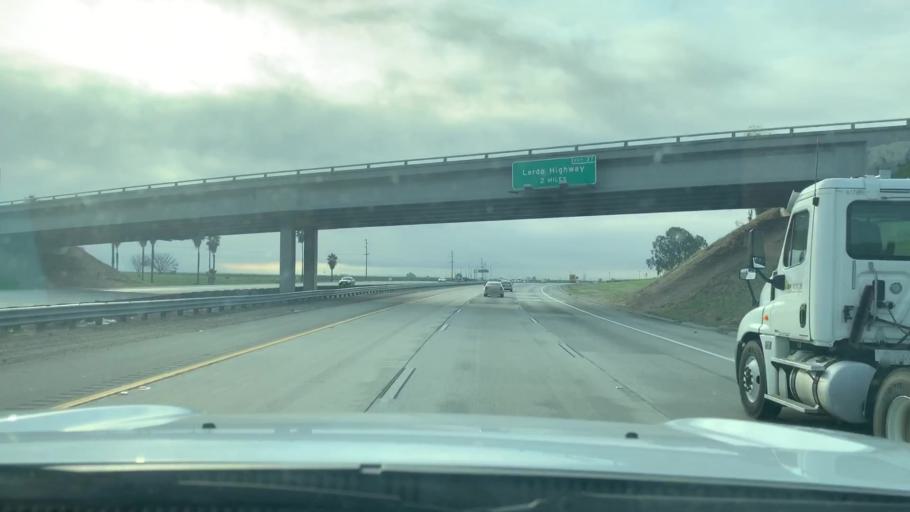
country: US
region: California
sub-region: Kern County
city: Shafter
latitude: 35.5301
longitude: -119.1900
